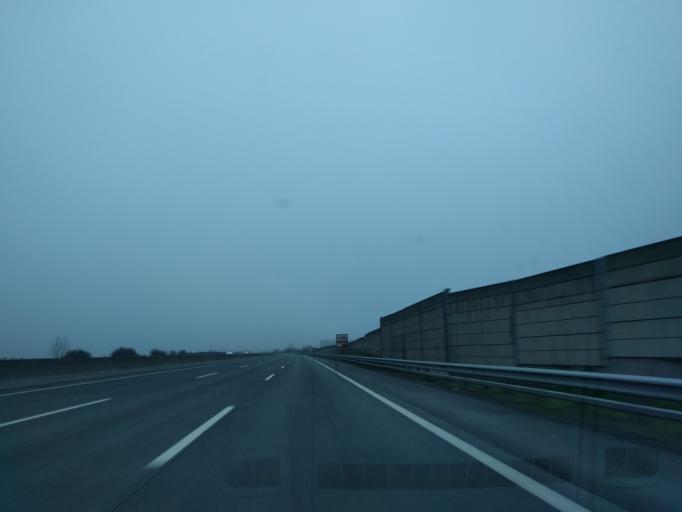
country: AT
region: Lower Austria
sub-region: Politischer Bezirk Amstetten
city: Amstetten
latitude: 48.1458
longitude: 14.8632
